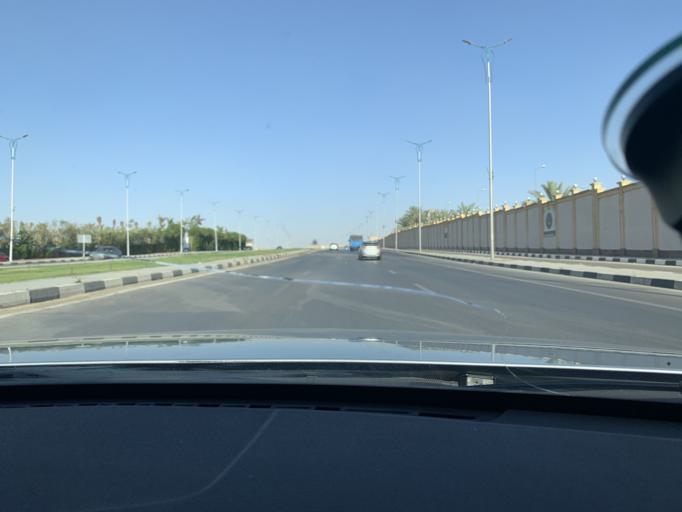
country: EG
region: Muhafazat al Qalyubiyah
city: Al Khankah
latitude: 30.0529
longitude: 31.4188
